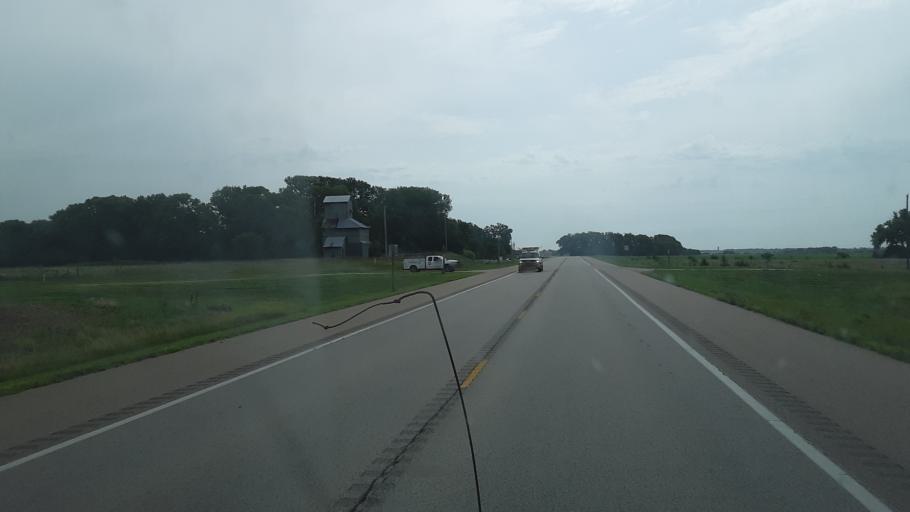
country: US
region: Kansas
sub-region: Stafford County
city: Stafford
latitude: 37.9843
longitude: -98.3634
